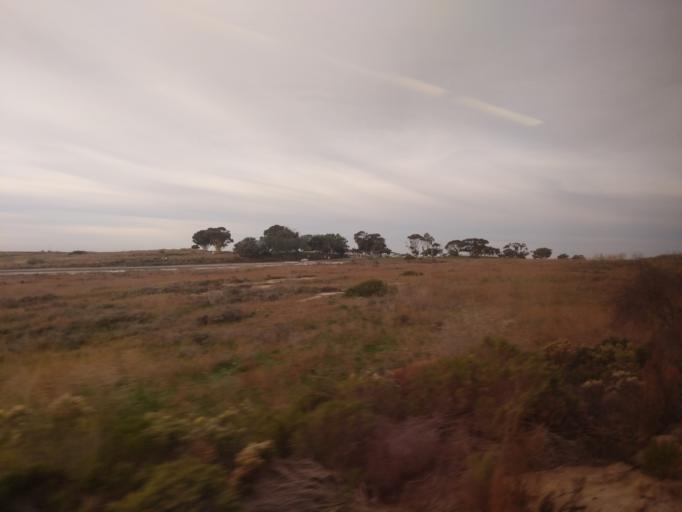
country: US
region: California
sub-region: San Diego County
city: Camp Pendleton South
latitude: 33.2726
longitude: -117.4390
